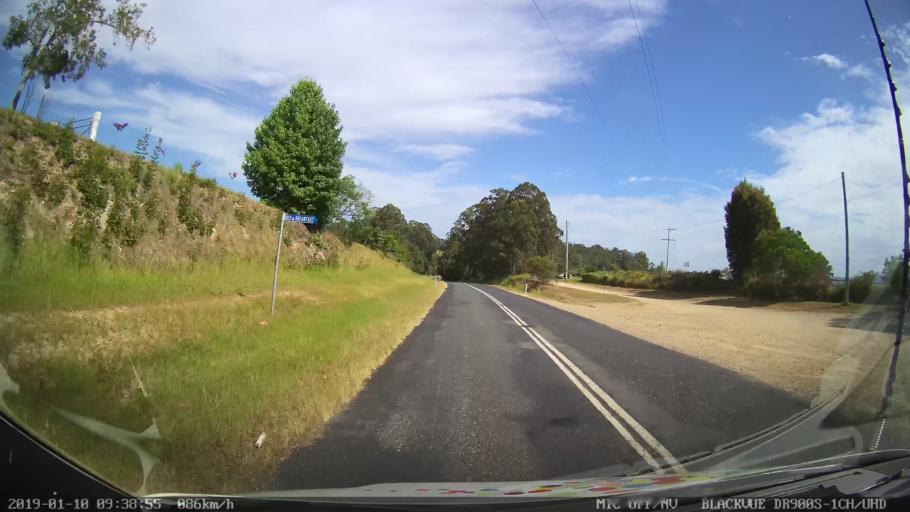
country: AU
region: New South Wales
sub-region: Coffs Harbour
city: Nana Glen
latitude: -30.1694
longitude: 153.0054
